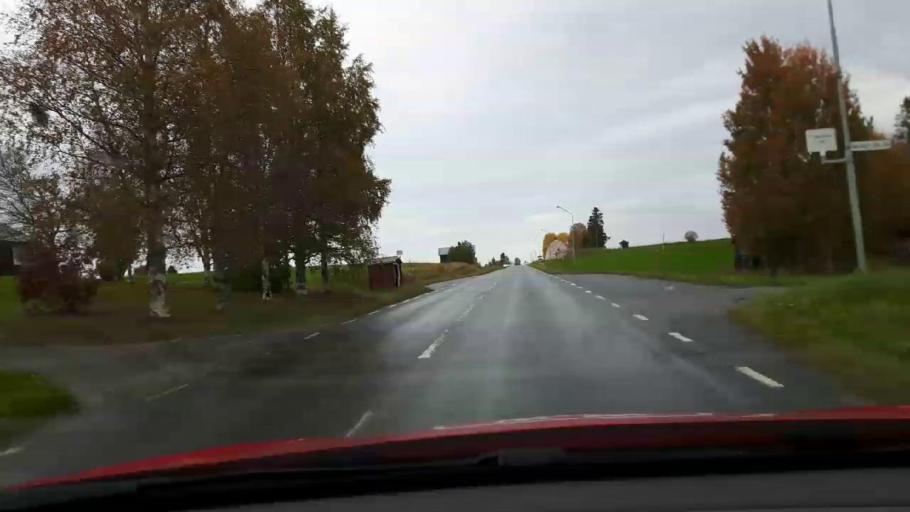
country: SE
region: Jaemtland
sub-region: Bergs Kommun
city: Hoverberg
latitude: 63.0077
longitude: 14.3402
